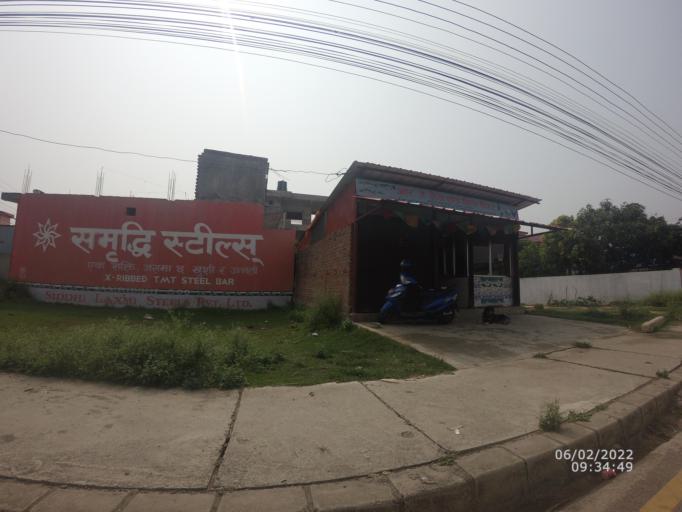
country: NP
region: Western Region
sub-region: Lumbini Zone
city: Bhairahawa
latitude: 27.4992
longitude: 83.4537
